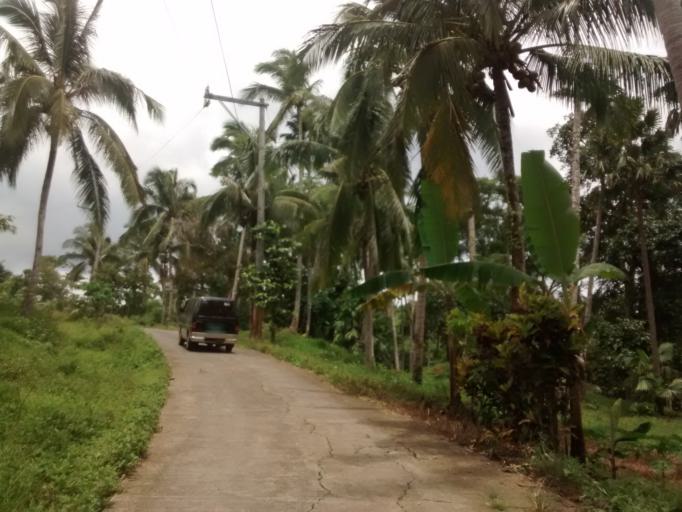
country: PH
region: Calabarzon
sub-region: Province of Quezon
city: Lucban
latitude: 14.1559
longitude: 121.5540
